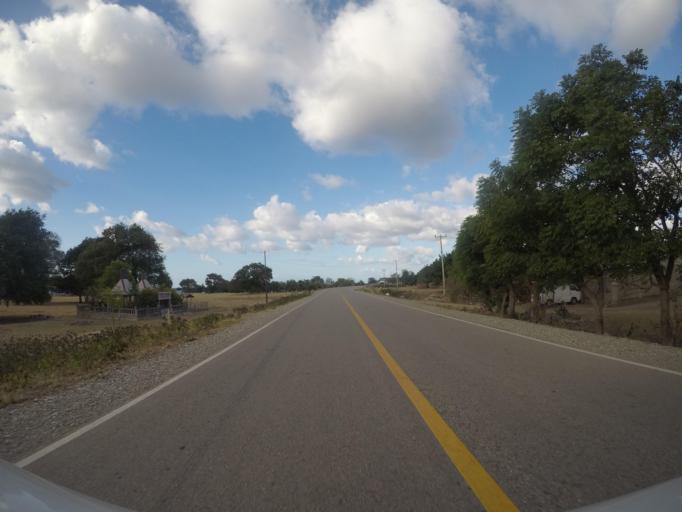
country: TL
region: Lautem
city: Lospalos
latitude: -8.3981
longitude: 126.8347
